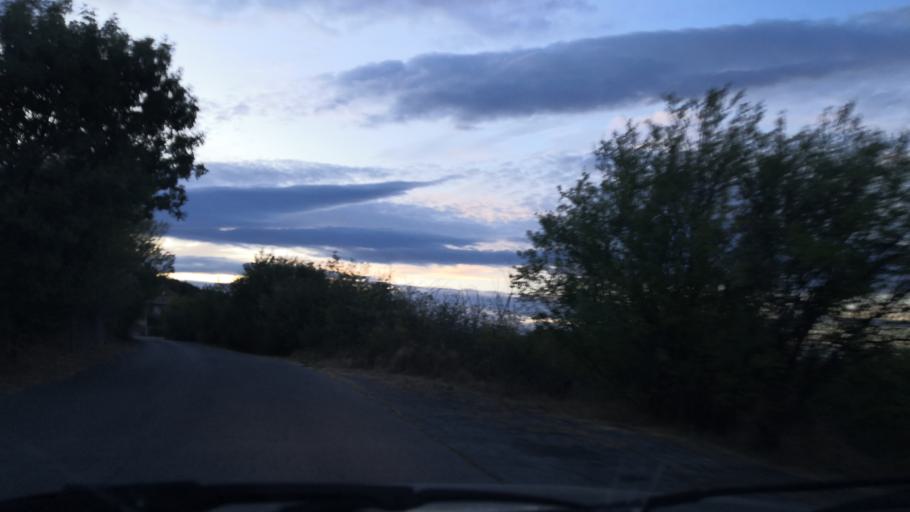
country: RO
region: Mehedinti
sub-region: Comuna Gogosu
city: Balta Verde
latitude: 44.3037
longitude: 22.5516
